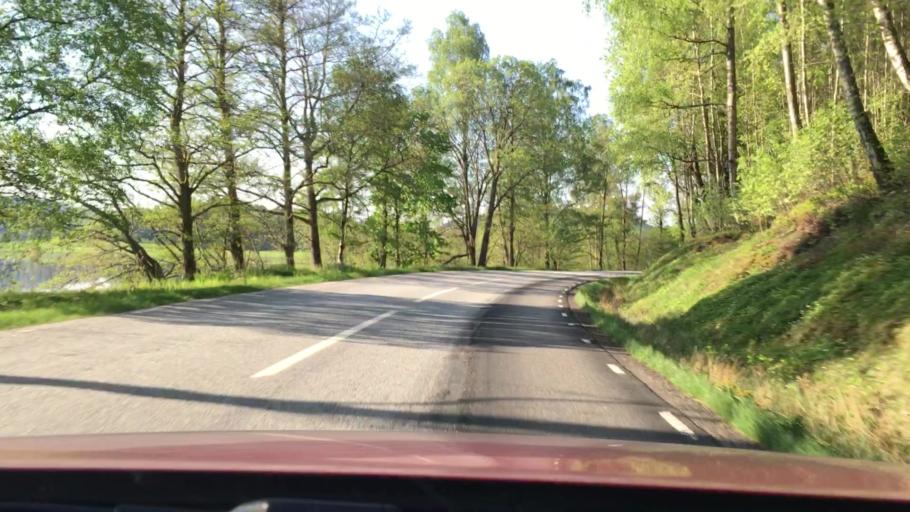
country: SE
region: Vaestra Goetaland
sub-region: Munkedals Kommun
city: Munkedal
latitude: 58.6252
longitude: 11.5602
